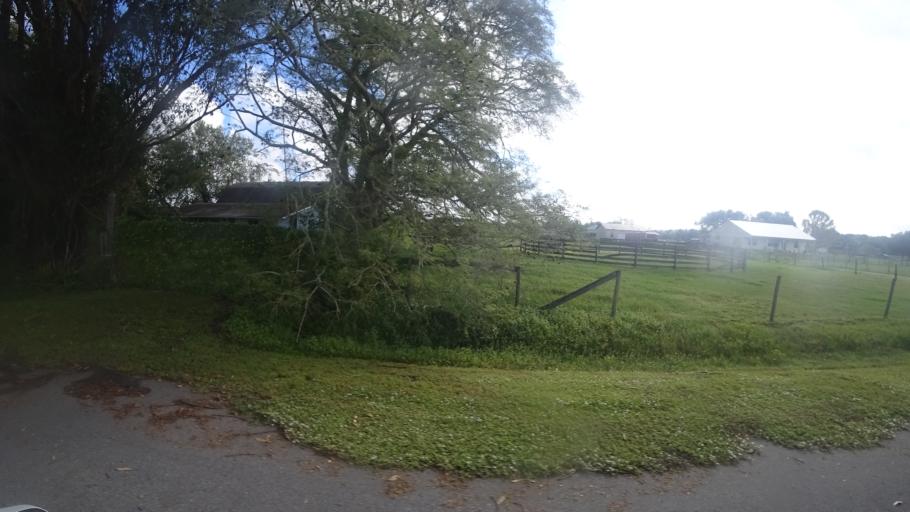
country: US
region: Florida
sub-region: Hillsborough County
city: Sun City Center
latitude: 27.5947
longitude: -82.3863
